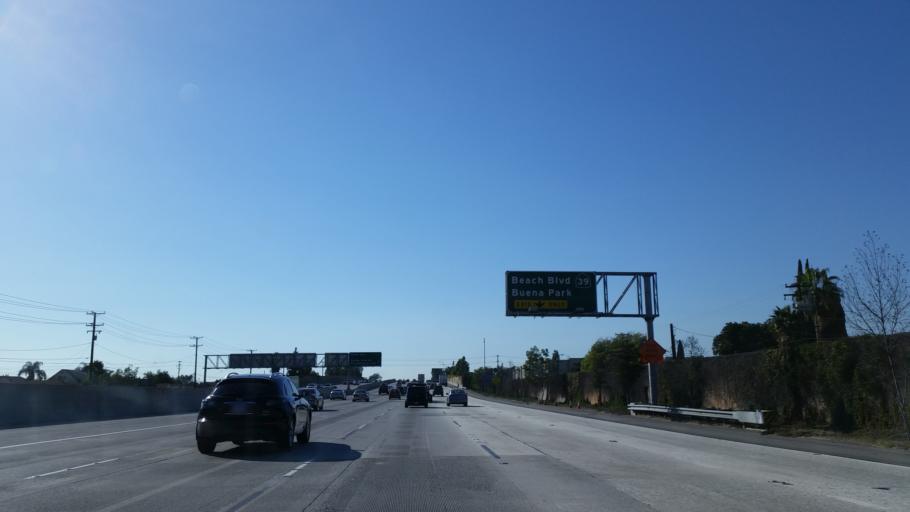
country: US
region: California
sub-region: Orange County
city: Buena Park
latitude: 33.8563
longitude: -117.9890
